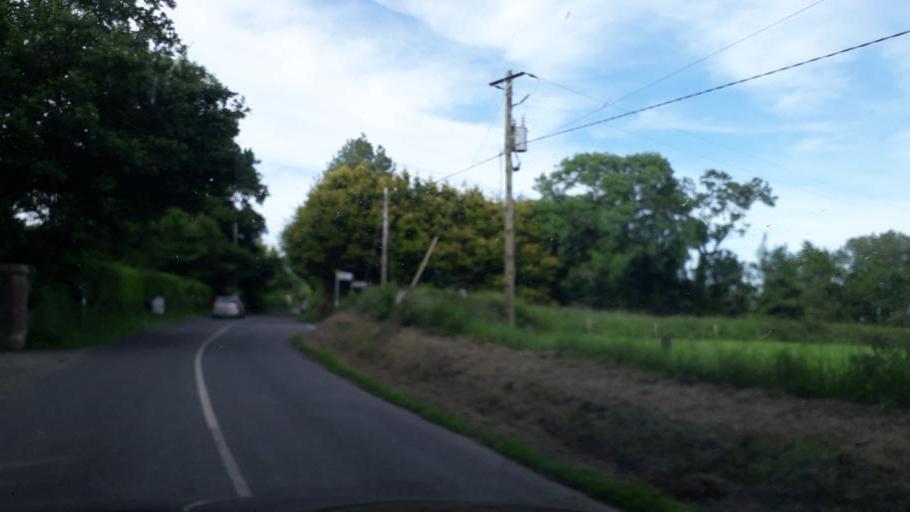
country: IE
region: Leinster
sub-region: Loch Garman
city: Courtown
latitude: 52.5574
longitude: -6.2359
